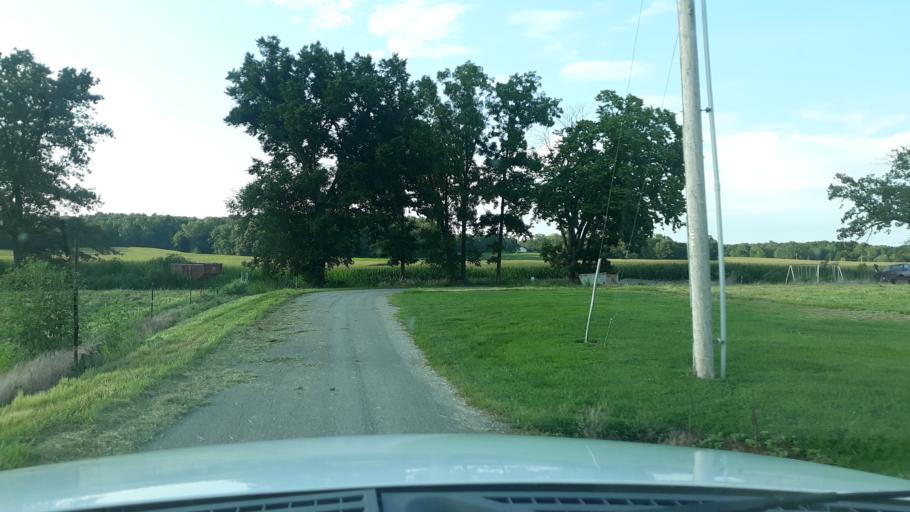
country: US
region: Illinois
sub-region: Saline County
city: Eldorado
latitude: 37.8337
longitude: -88.5165
